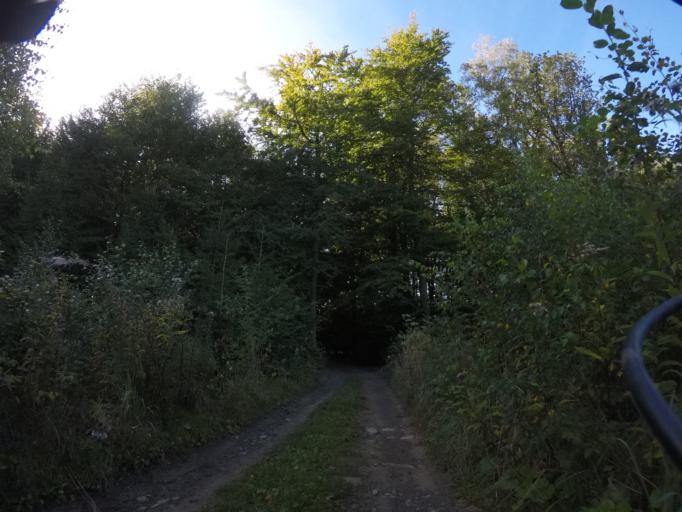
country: BE
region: Wallonia
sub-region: Province du Luxembourg
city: Fauvillers
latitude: 49.9269
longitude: 5.6575
